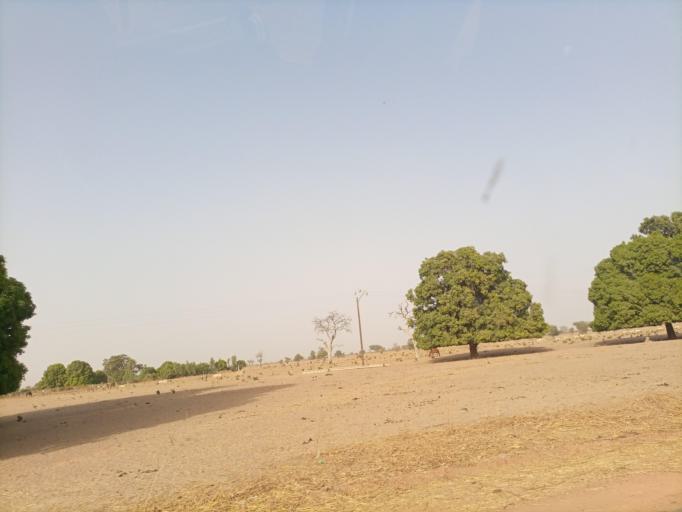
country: SN
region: Fatick
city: Passi
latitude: 14.0324
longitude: -16.3123
